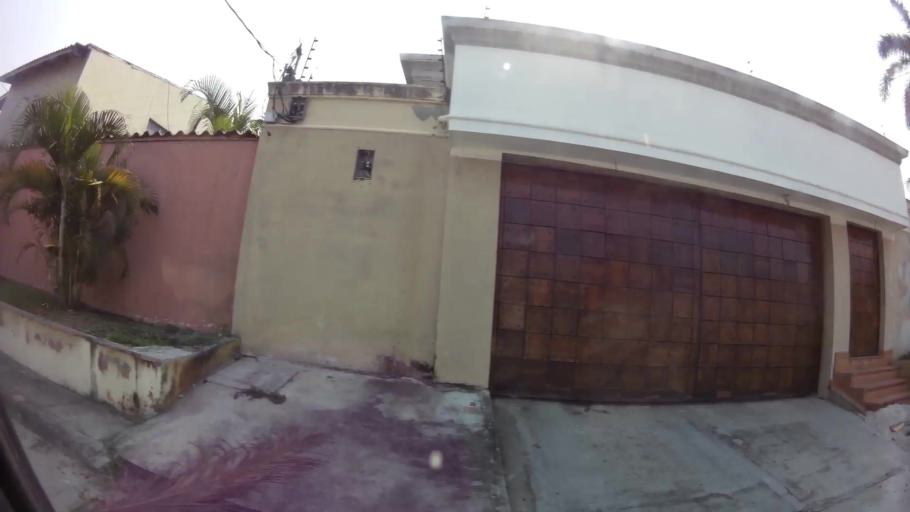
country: HN
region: Cortes
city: Armenta
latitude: 15.4963
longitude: -88.0421
